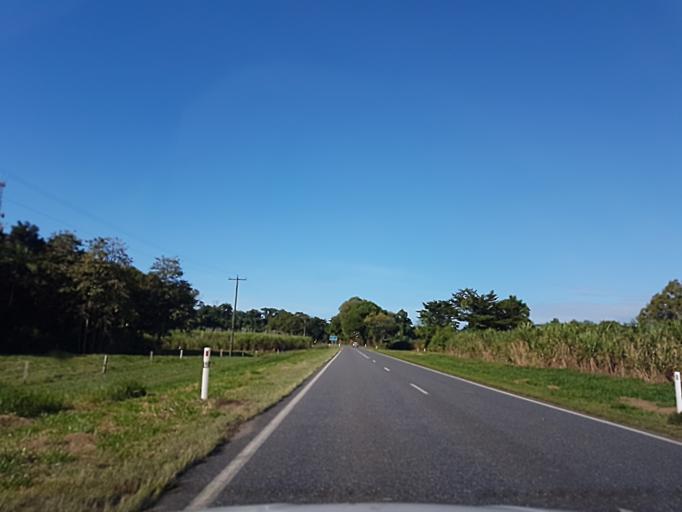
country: AU
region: Queensland
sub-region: Cairns
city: Port Douglas
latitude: -16.4361
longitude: 145.3835
